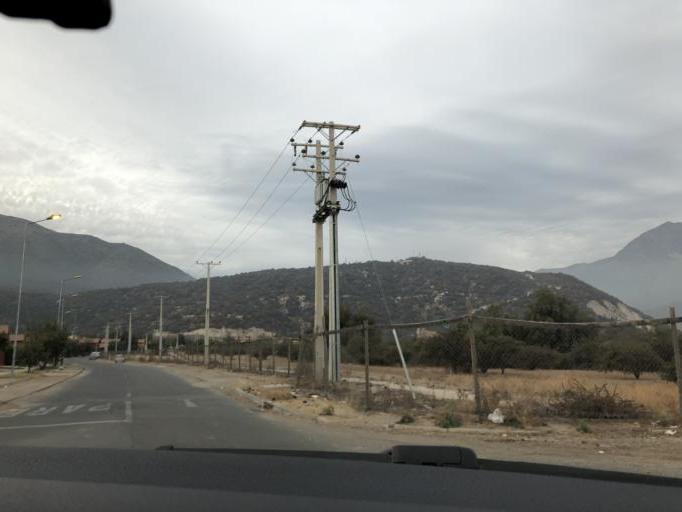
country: CL
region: Santiago Metropolitan
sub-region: Provincia de Cordillera
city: Puente Alto
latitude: -33.5912
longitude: -70.5130
